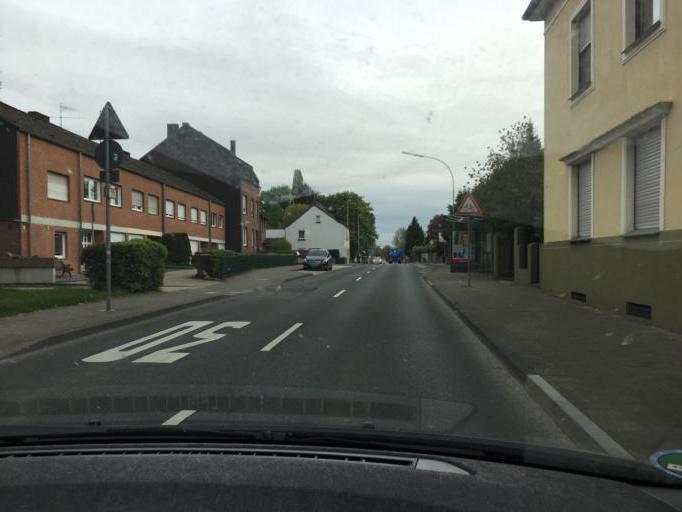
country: DE
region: North Rhine-Westphalia
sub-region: Regierungsbezirk Dusseldorf
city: Monchengladbach
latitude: 51.1143
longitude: 6.4128
